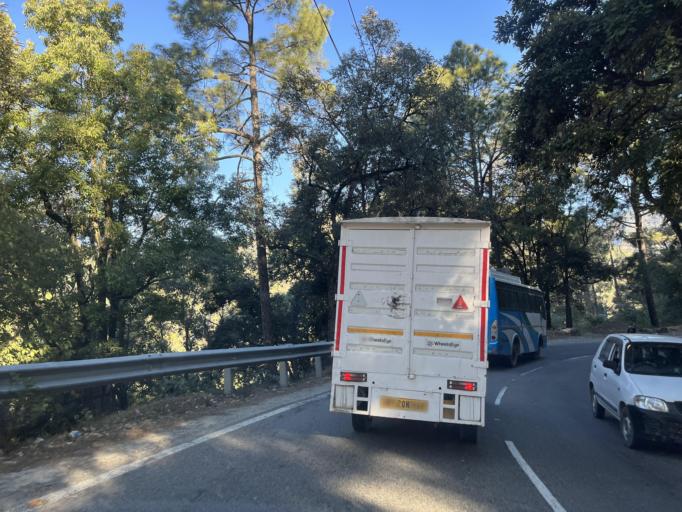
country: IN
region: Uttarakhand
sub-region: Naini Tal
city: Bhowali
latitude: 29.3995
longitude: 79.5084
